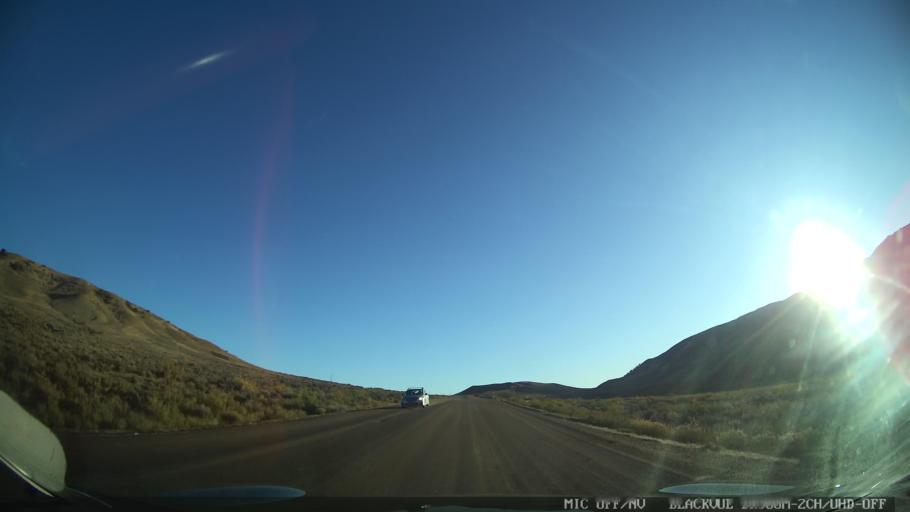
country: US
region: Colorado
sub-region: Grand County
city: Kremmling
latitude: 40.0345
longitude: -106.3785
